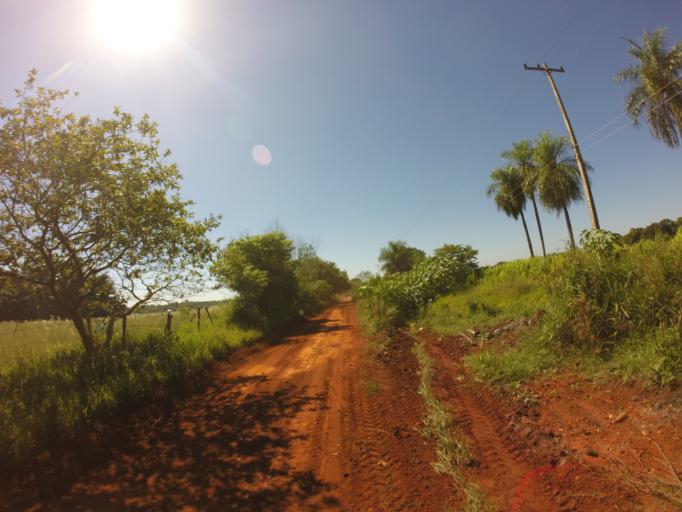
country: PY
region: Alto Parana
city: Ciudad del Este
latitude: -25.4329
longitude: -54.6602
